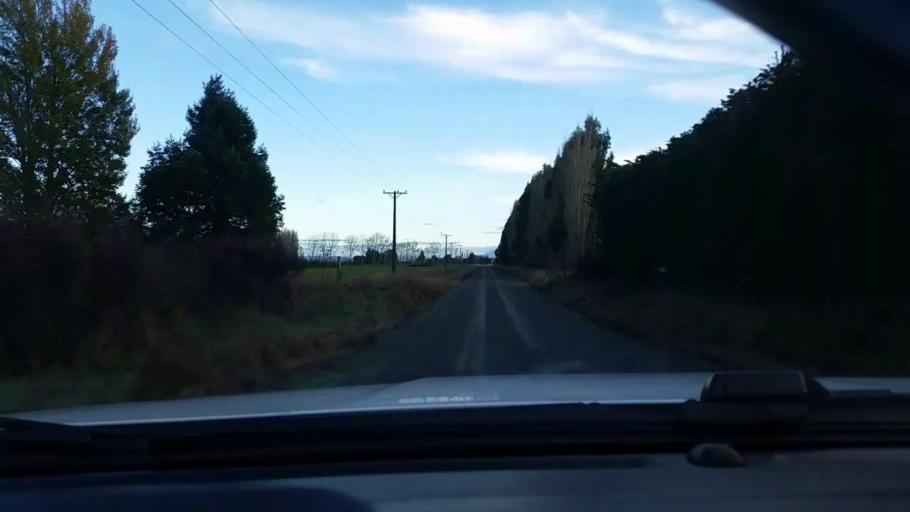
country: NZ
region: Southland
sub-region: Southland District
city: Winton
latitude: -46.1493
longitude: 168.2548
